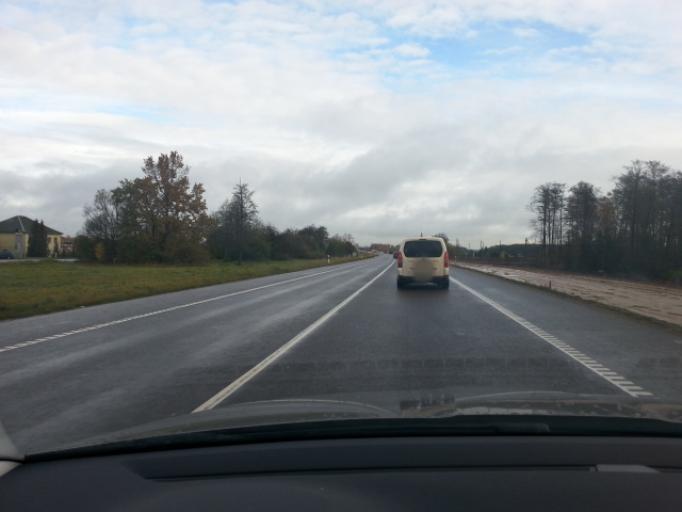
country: LT
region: Marijampoles apskritis
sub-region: Marijampole Municipality
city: Marijampole
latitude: 54.6041
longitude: 23.4056
